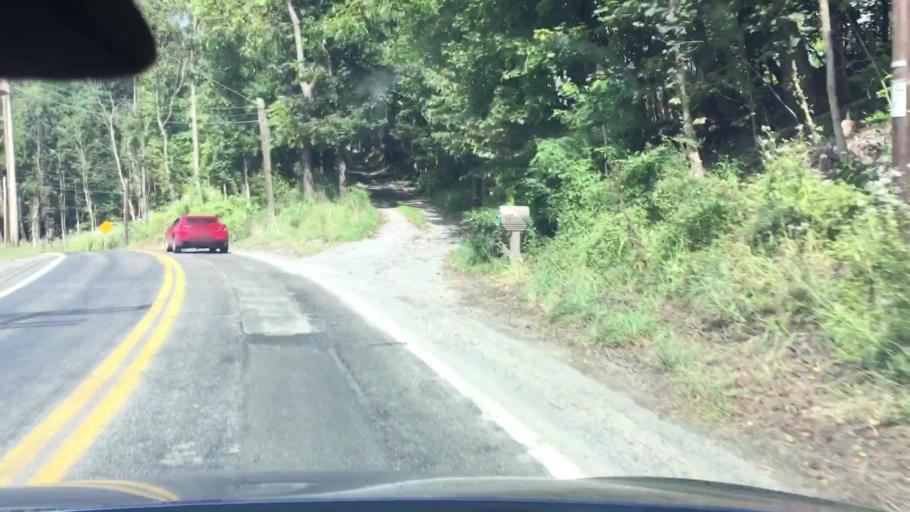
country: US
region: Pennsylvania
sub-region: Allegheny County
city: Russellton
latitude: 40.5819
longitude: -79.8249
